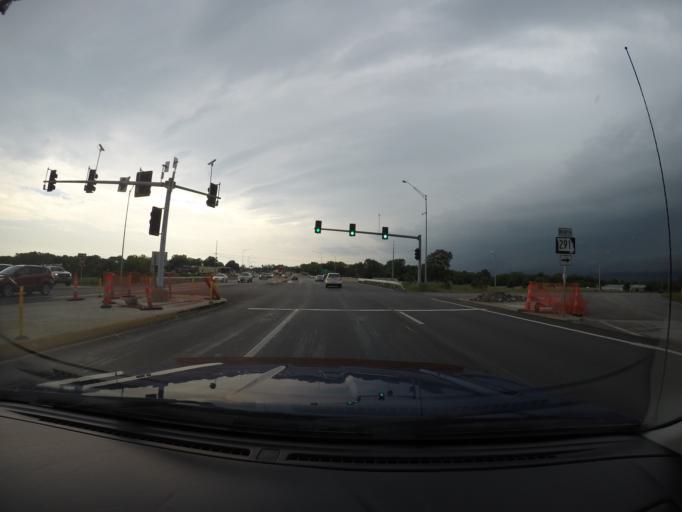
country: US
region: Missouri
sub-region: Jackson County
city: East Independence
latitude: 39.1176
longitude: -94.3840
